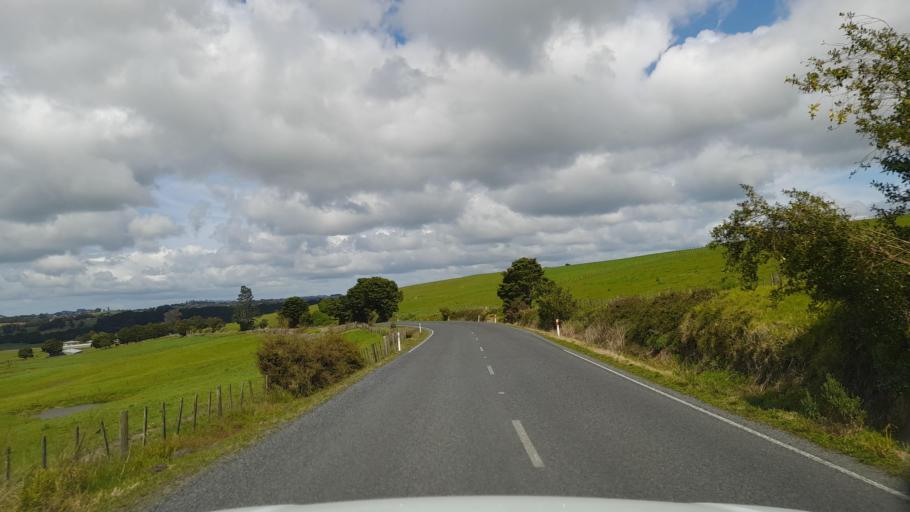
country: NZ
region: Northland
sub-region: Whangarei
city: Maungatapere
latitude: -35.6523
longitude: 174.1249
